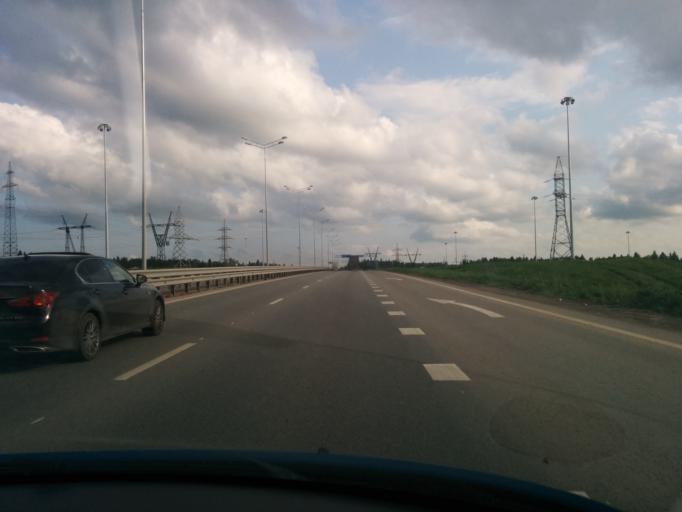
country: RU
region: Perm
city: Novyye Lyady
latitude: 58.0479
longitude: 56.4296
